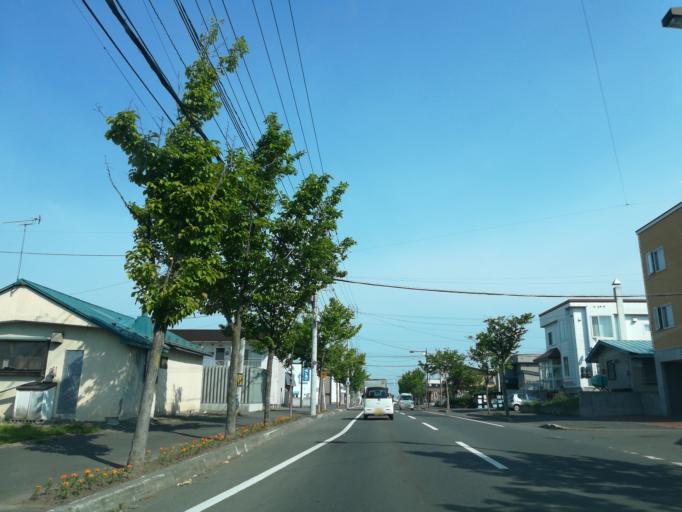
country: JP
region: Hokkaido
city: Iwamizawa
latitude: 43.2058
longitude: 141.7786
